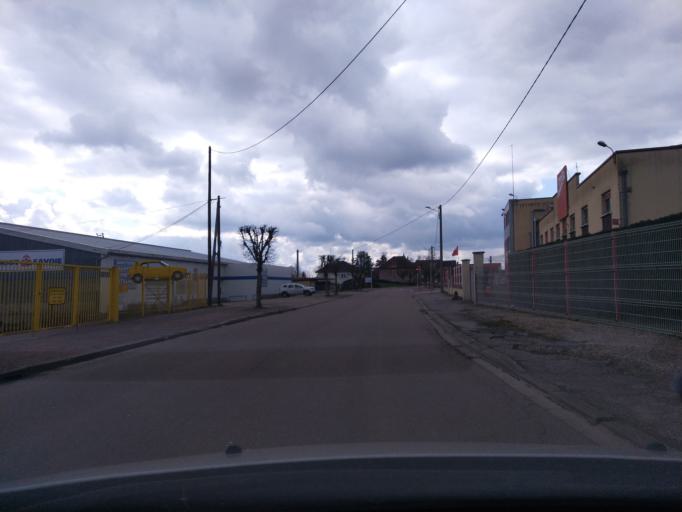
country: FR
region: Bourgogne
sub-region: Departement de l'Yonne
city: Avallon
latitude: 47.4950
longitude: 3.9233
